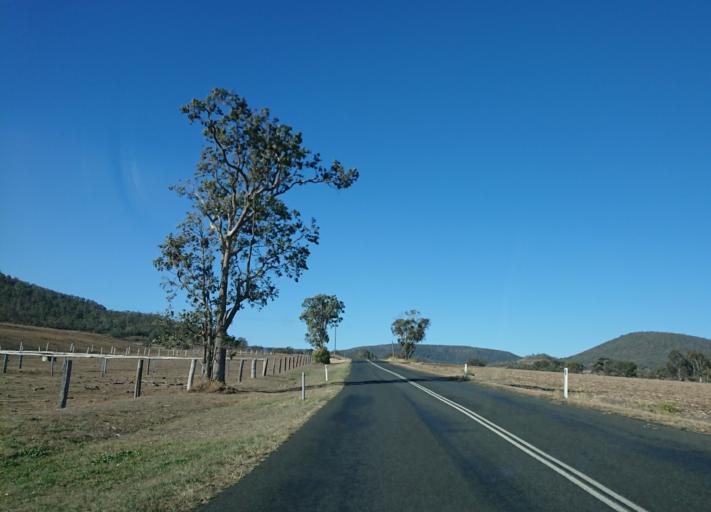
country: AU
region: Queensland
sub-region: Toowoomba
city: Top Camp
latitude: -27.8394
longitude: 152.0720
